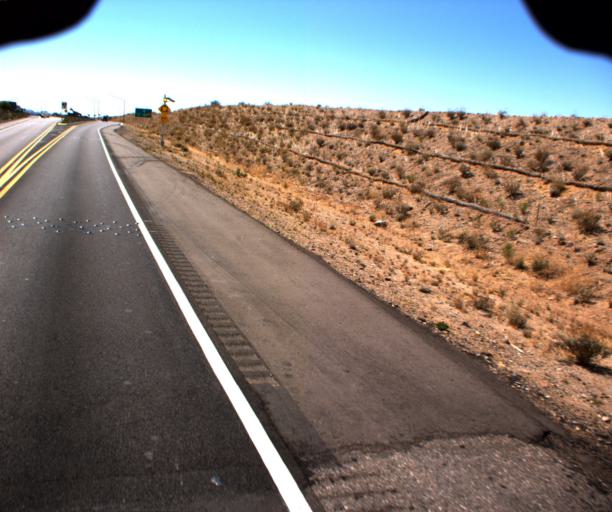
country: US
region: Arizona
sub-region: Maricopa County
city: Wickenburg
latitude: 34.0195
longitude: -112.8014
